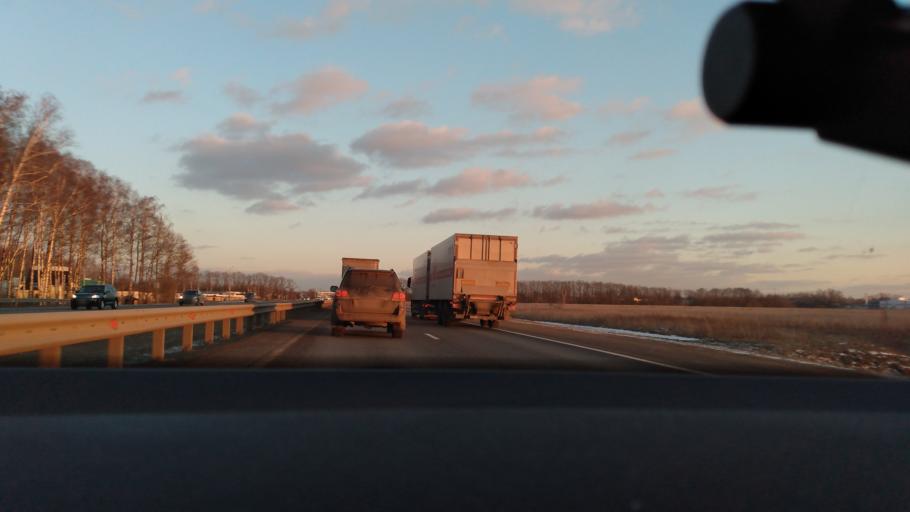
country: RU
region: Moskovskaya
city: Raduzhnyy
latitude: 55.1489
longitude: 38.7166
